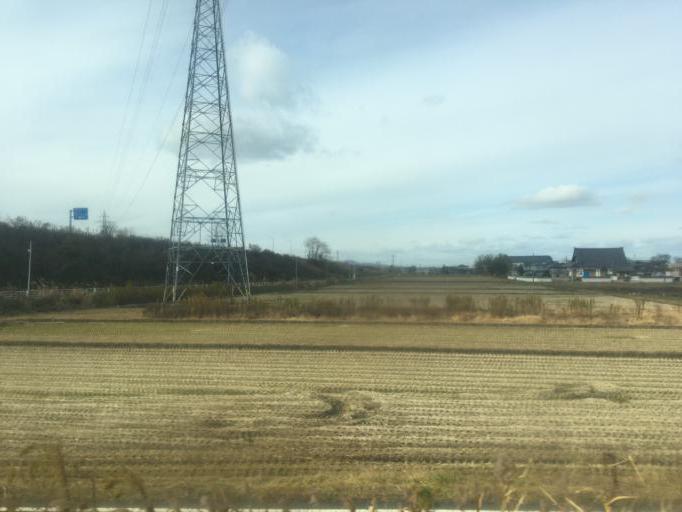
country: JP
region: Akita
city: Tenno
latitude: 39.8618
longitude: 140.0591
